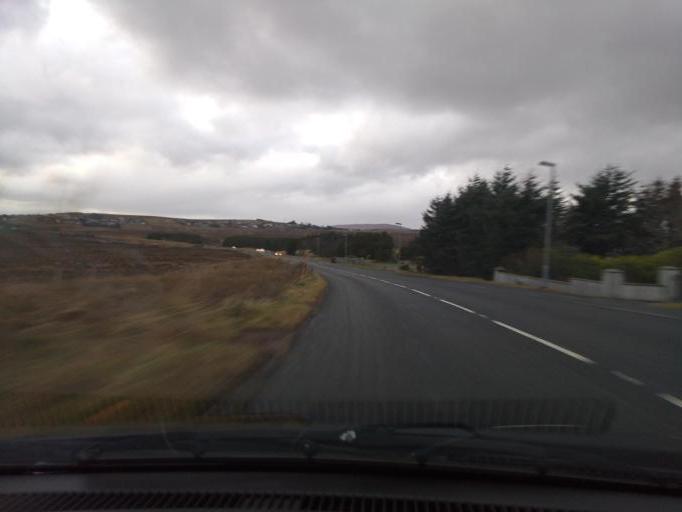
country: GB
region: Scotland
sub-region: Eilean Siar
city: Isle of Lewis
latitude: 58.2446
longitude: -6.3595
